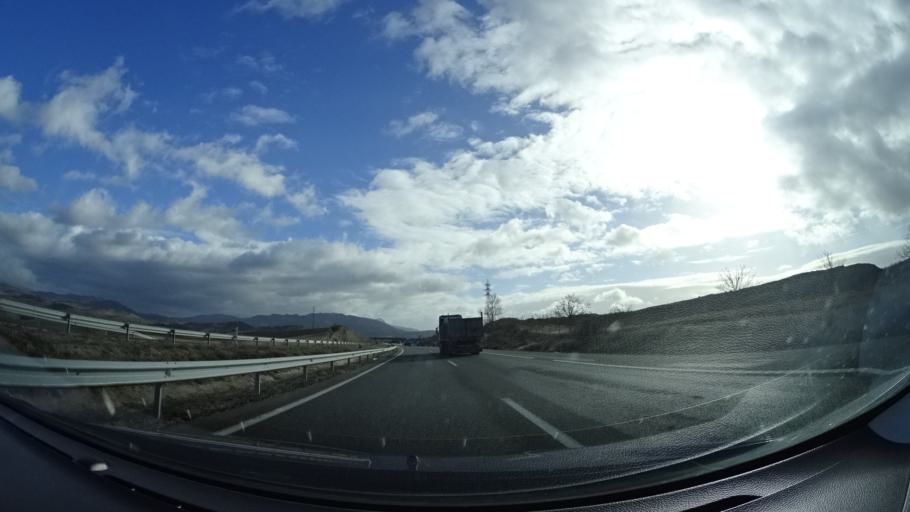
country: ES
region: Basque Country
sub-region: Provincia de Alava
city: Arminon
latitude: 42.6998
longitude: -2.8980
